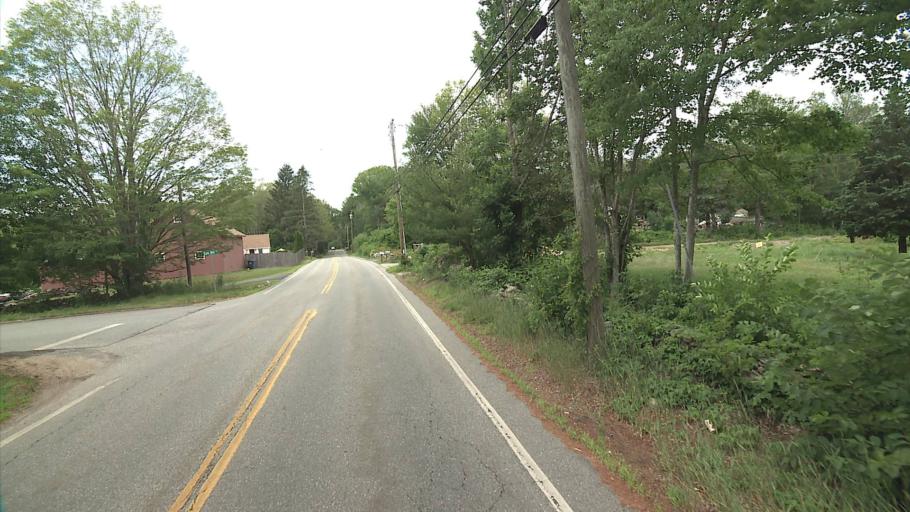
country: US
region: Connecticut
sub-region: New London County
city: Ledyard Center
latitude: 41.4477
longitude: -71.9846
